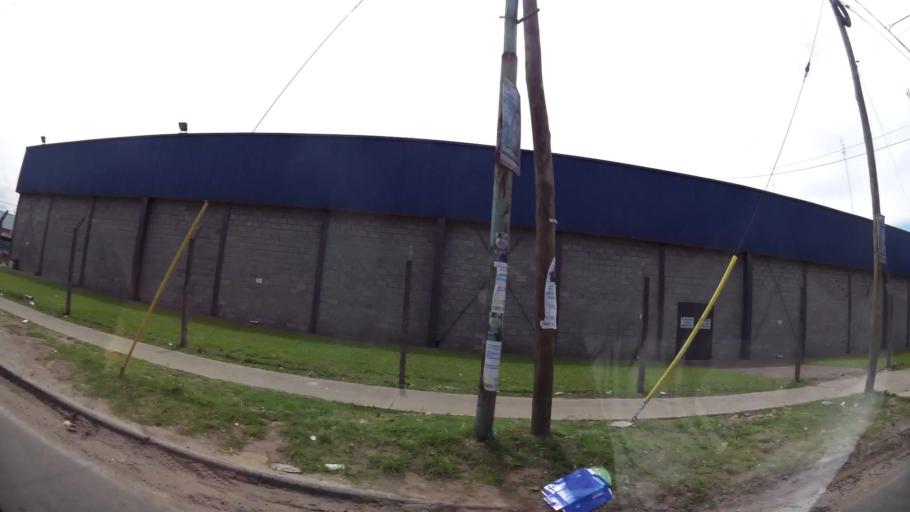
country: AR
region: Buenos Aires
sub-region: Partido de Quilmes
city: Quilmes
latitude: -34.7799
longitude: -58.2785
